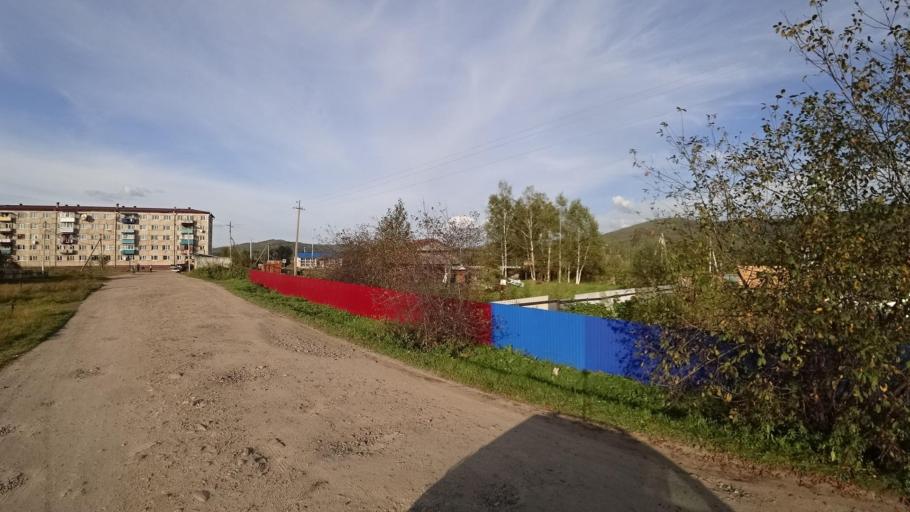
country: RU
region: Jewish Autonomous Oblast
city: Kul'dur
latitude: 49.2002
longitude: 131.6262
